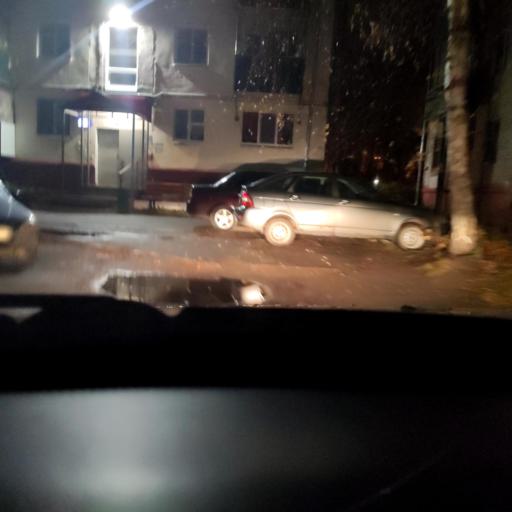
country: RU
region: Perm
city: Kultayevo
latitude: 58.0076
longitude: 55.9666
